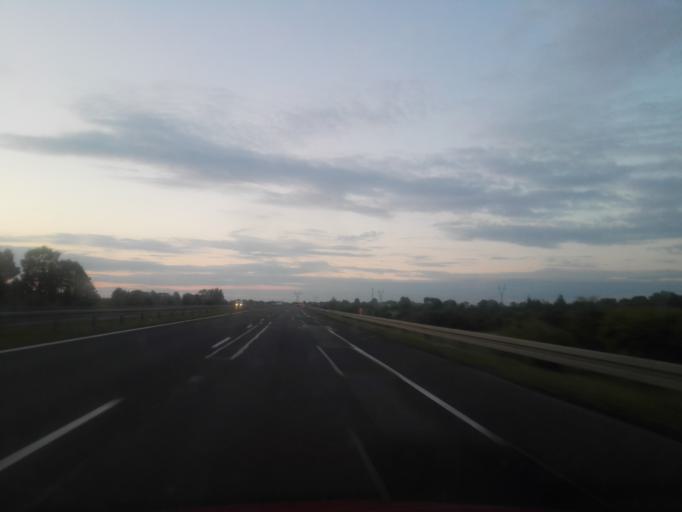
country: PL
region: Lodz Voivodeship
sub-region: Powiat piotrkowski
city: Wola Krzysztoporska
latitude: 51.2796
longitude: 19.5349
